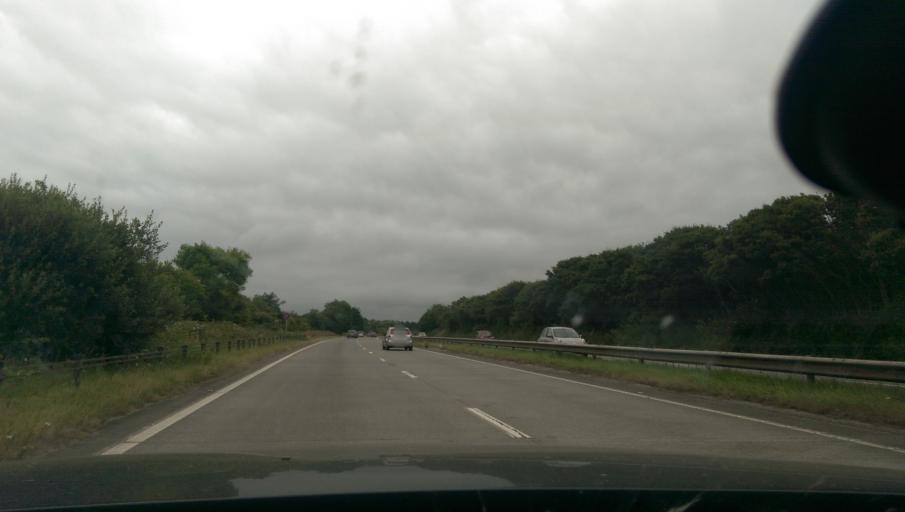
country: GB
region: England
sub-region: Cornwall
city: Marazion
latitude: 50.1323
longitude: -5.5029
